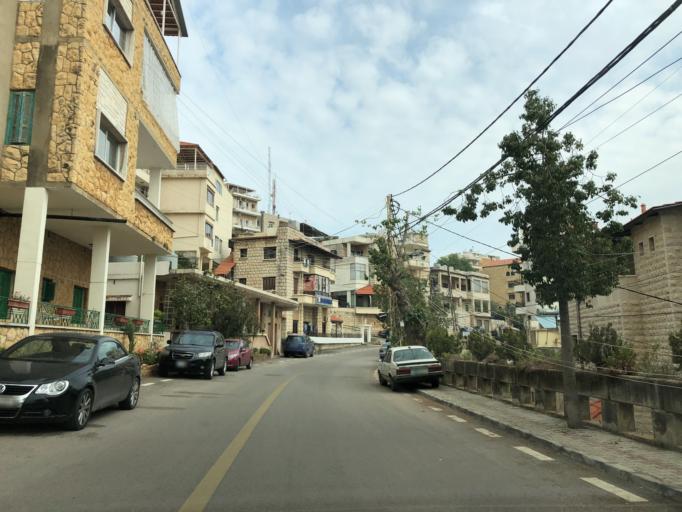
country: LB
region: Mont-Liban
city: Jdaidet el Matn
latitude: 33.8636
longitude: 35.6054
